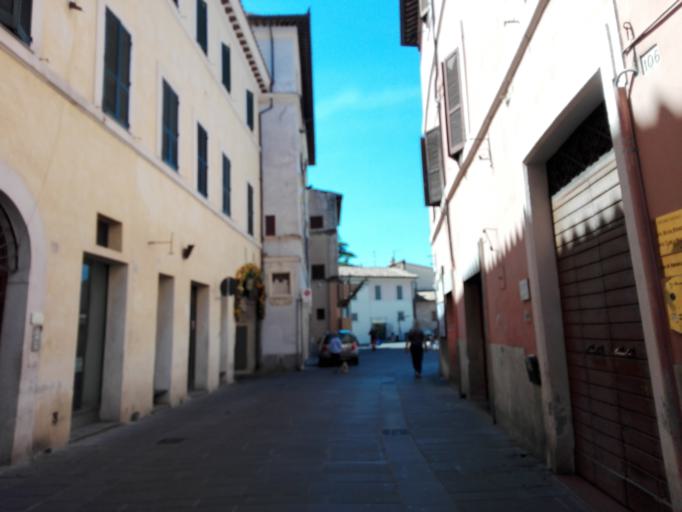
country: IT
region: Umbria
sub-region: Provincia di Perugia
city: Foligno
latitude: 42.9537
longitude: 12.7014
